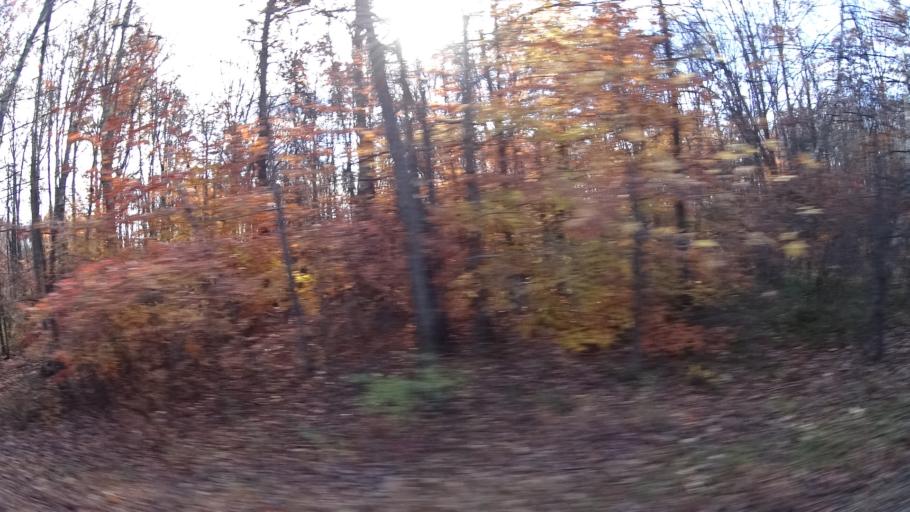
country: US
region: New Jersey
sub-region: Union County
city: Berkeley Heights
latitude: 40.7215
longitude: -74.4919
